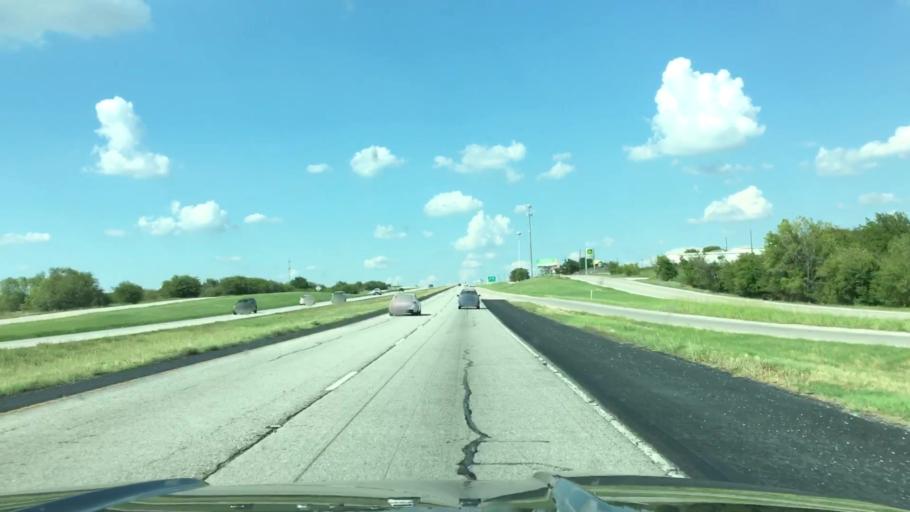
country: US
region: Texas
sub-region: Wise County
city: Rhome
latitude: 33.0584
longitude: -97.4777
